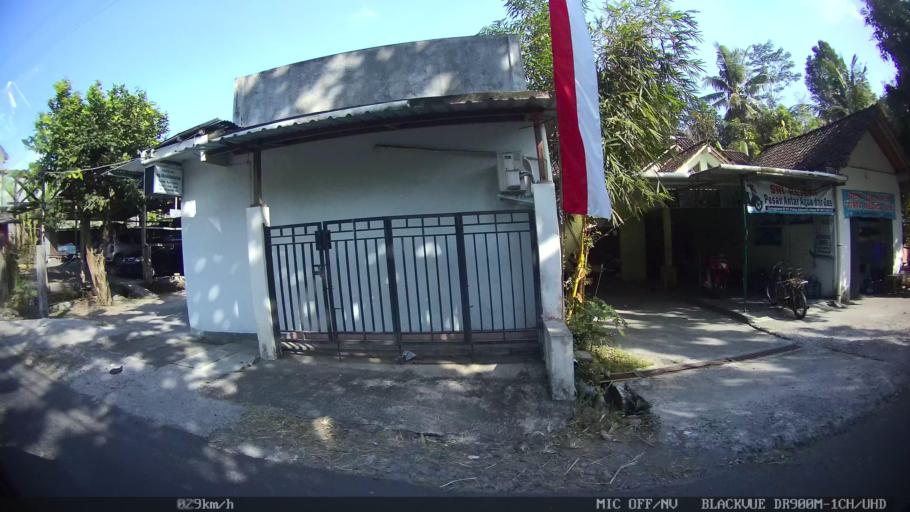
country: ID
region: Daerah Istimewa Yogyakarta
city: Godean
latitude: -7.8192
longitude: 110.2750
